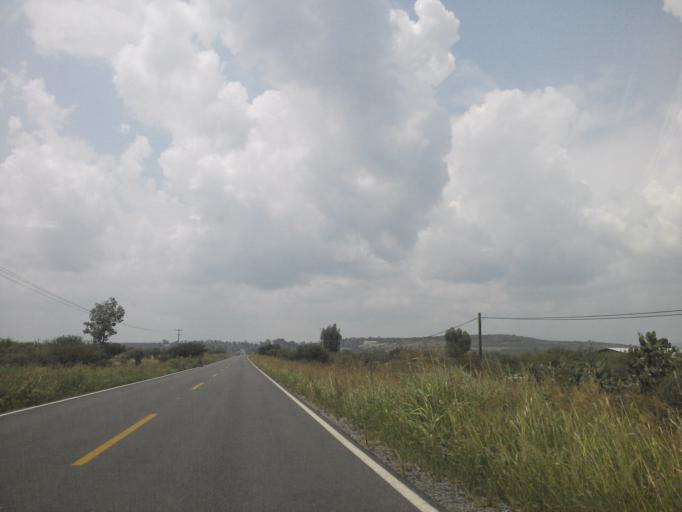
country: MX
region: Guanajuato
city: Ciudad Manuel Doblado
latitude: 20.8134
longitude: -101.9984
